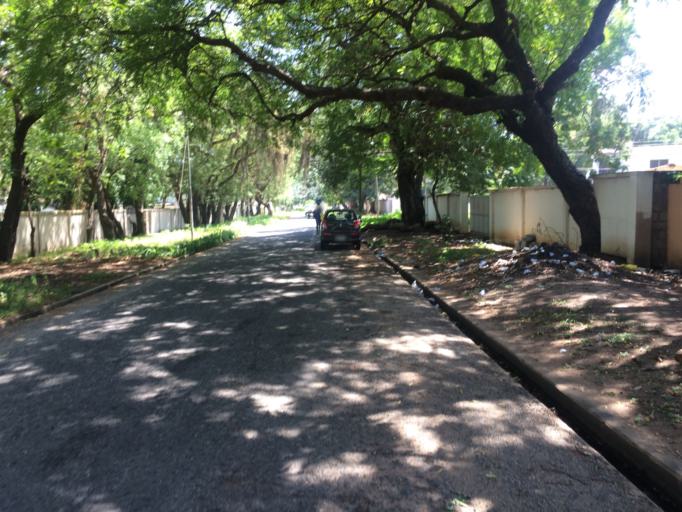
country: GH
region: Greater Accra
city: Accra
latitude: 5.5633
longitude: -0.1902
